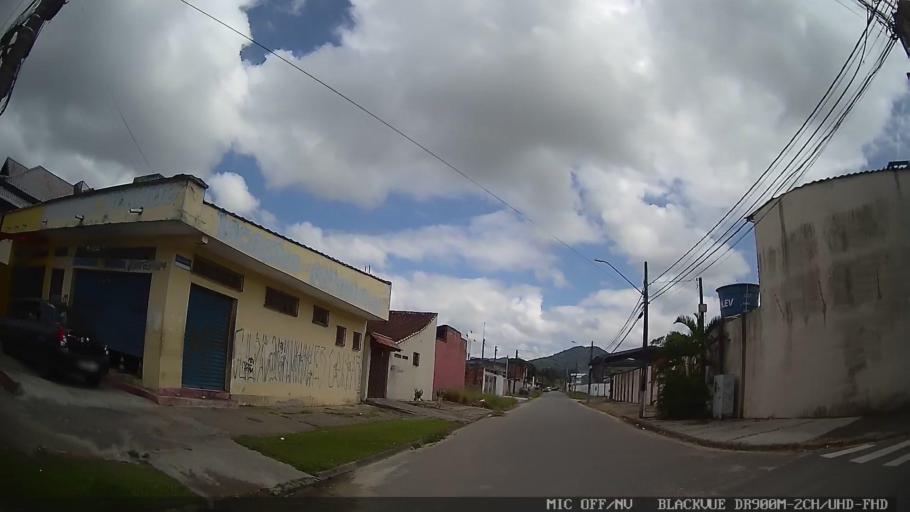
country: BR
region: Sao Paulo
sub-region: Peruibe
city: Peruibe
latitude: -24.2954
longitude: -47.0215
